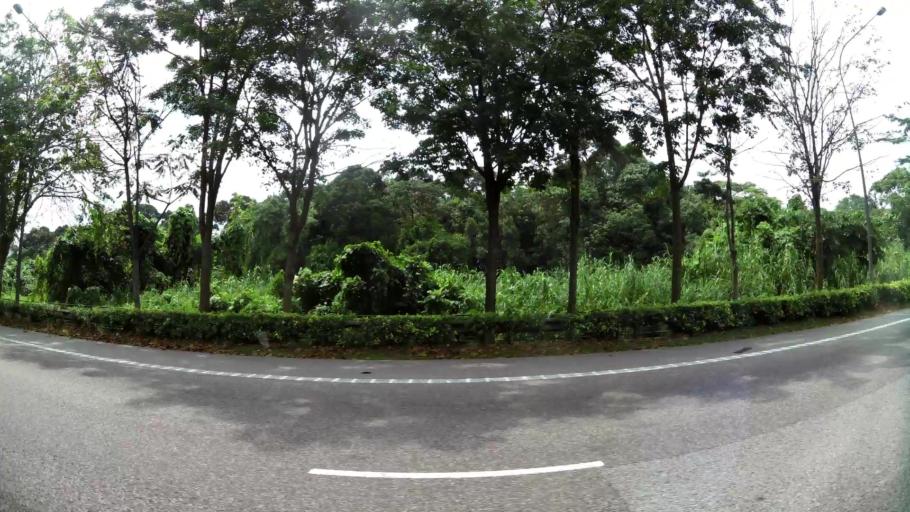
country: MY
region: Johor
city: Johor Bahru
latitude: 1.3940
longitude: 103.7739
